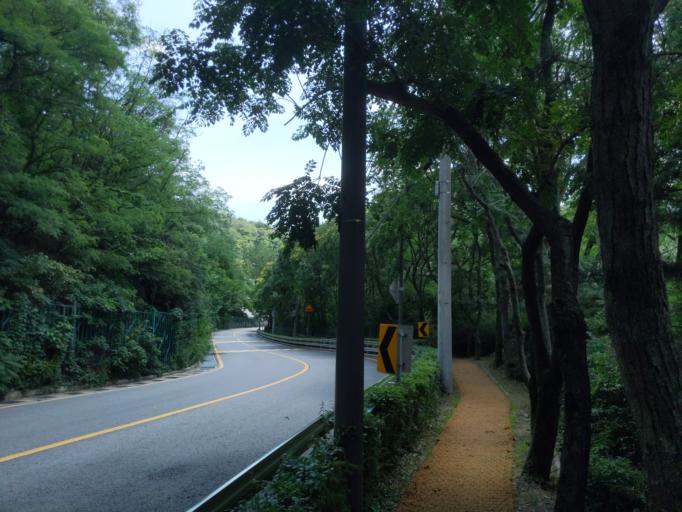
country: KR
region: Seoul
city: Seoul
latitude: 37.5987
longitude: 126.9734
